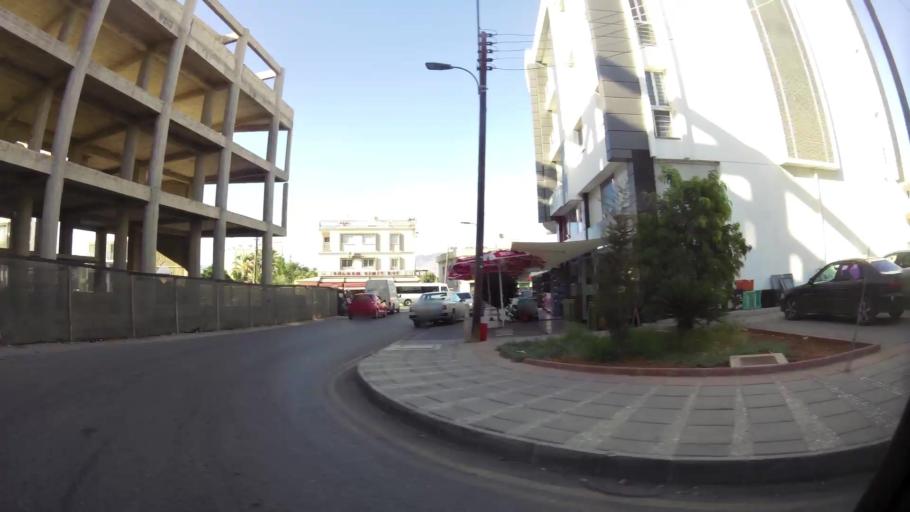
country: CY
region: Lefkosia
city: Nicosia
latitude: 35.1991
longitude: 33.3375
